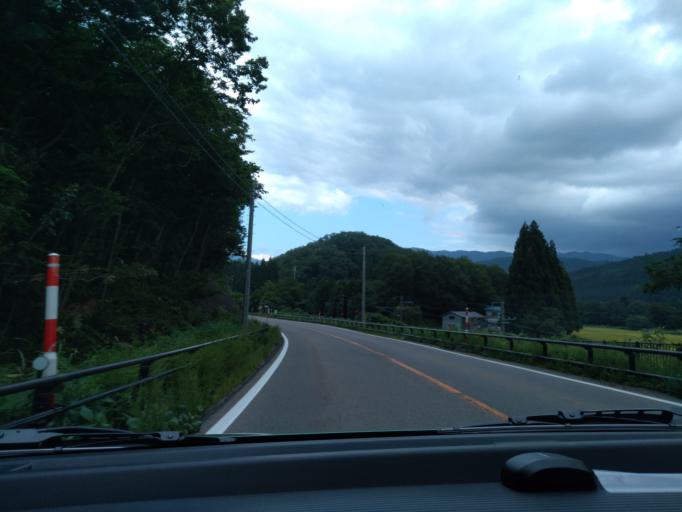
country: JP
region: Akita
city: Kakunodatemachi
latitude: 39.6660
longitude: 140.6887
